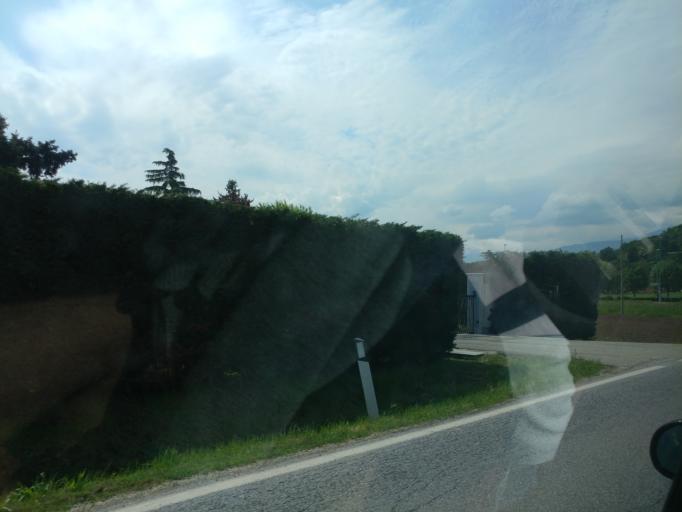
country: IT
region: Piedmont
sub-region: Provincia di Torino
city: Cavour
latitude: 44.7826
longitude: 7.3836
